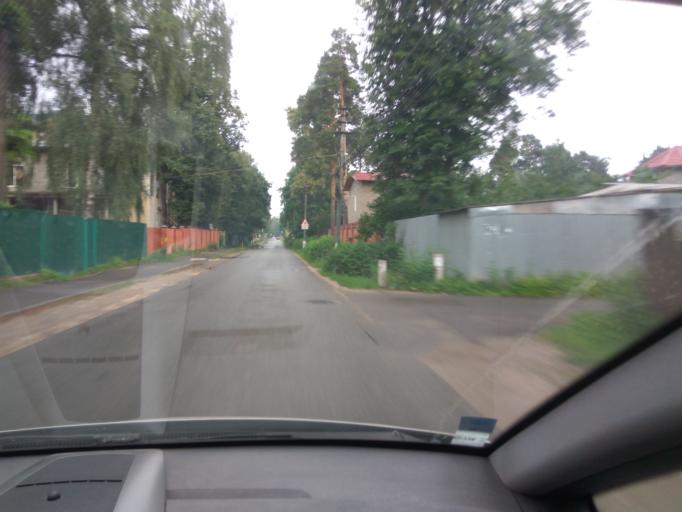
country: RU
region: Moskovskaya
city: Bykovo
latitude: 55.6306
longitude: 38.0684
